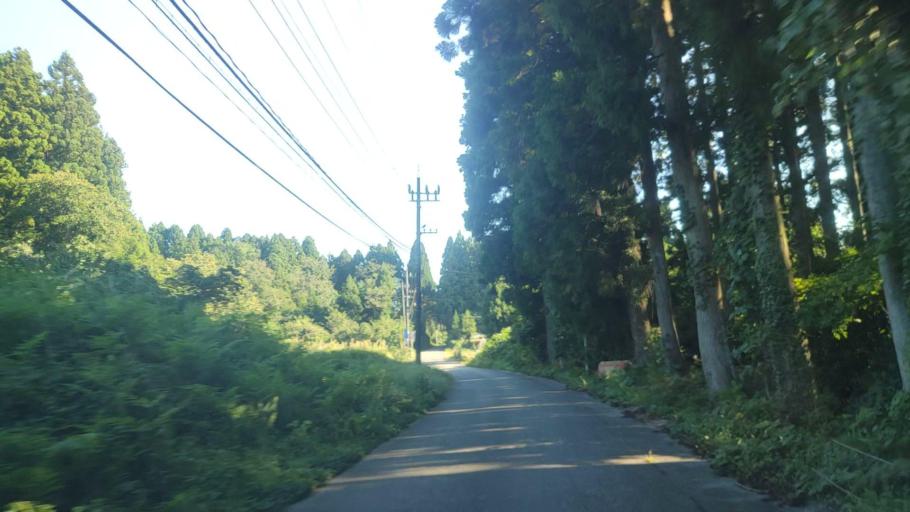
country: JP
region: Ishikawa
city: Nanao
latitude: 37.1363
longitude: 136.9090
